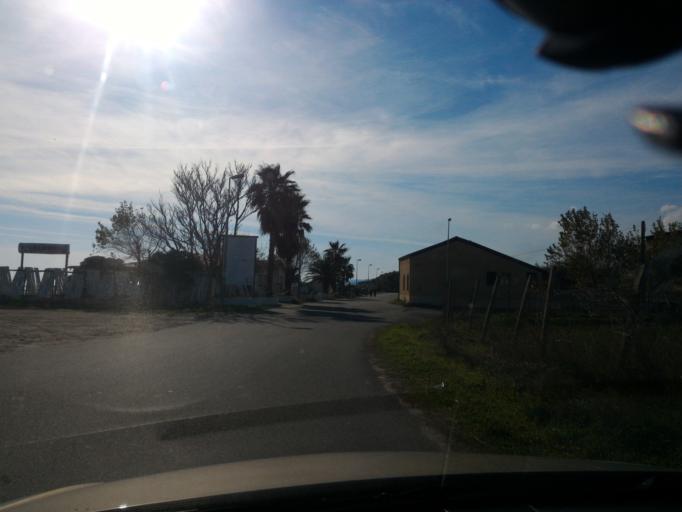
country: IT
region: Calabria
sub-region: Provincia di Crotone
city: Ciro Marina
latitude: 39.3553
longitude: 17.1298
